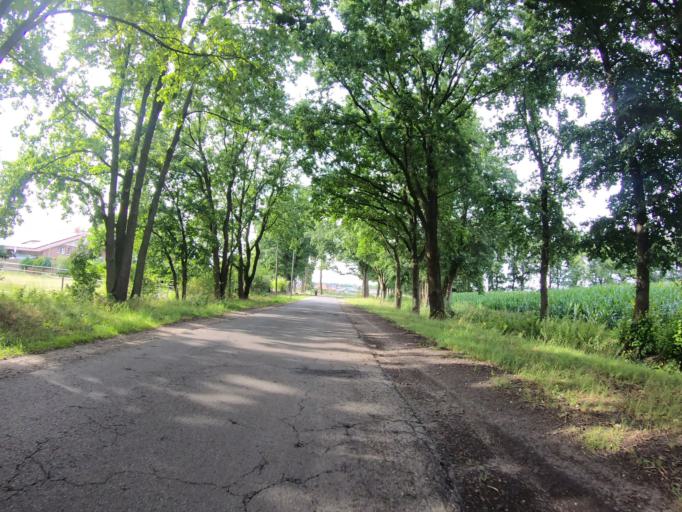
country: DE
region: Lower Saxony
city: Gifhorn
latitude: 52.5002
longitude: 10.5875
